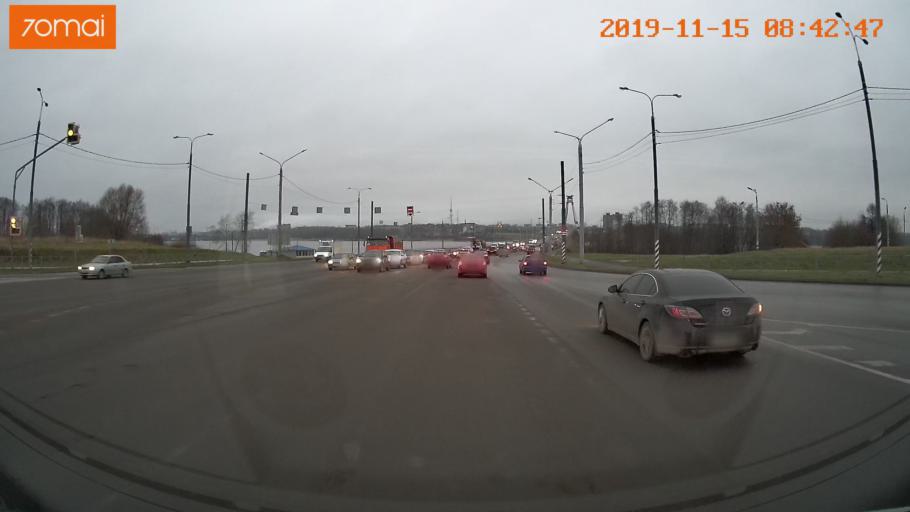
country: RU
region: Vologda
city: Cherepovets
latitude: 59.1056
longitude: 37.9062
